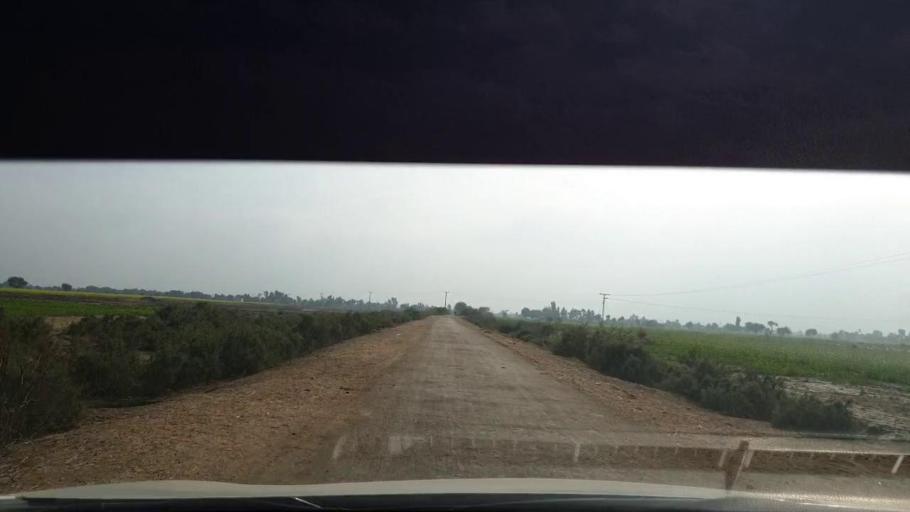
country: PK
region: Sindh
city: Berani
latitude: 25.7644
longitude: 68.8764
